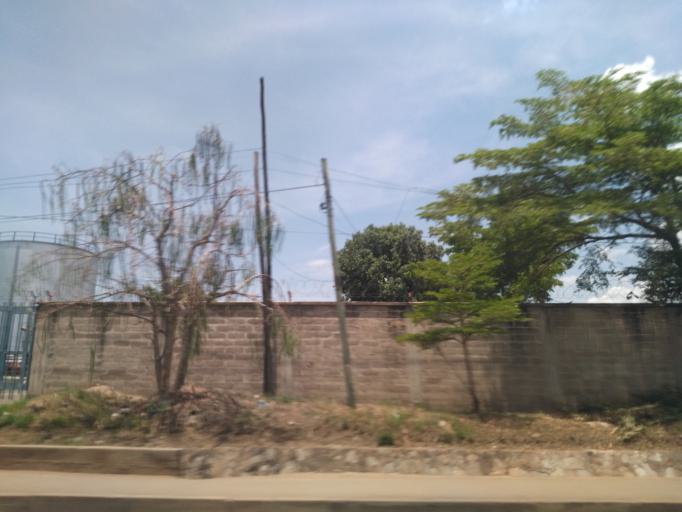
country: TZ
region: Mwanza
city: Mwanza
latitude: -2.5387
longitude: 32.9042
